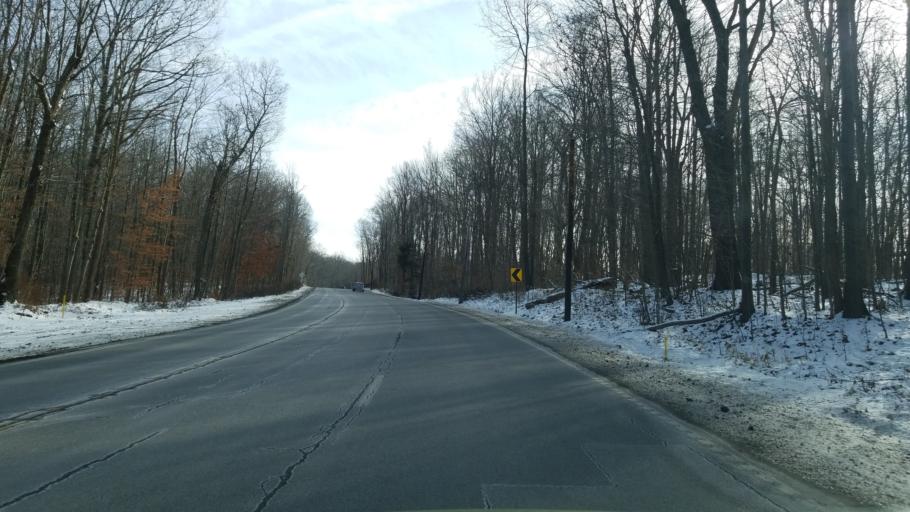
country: US
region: Pennsylvania
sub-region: Clearfield County
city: Treasure Lake
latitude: 41.1901
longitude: -78.5550
